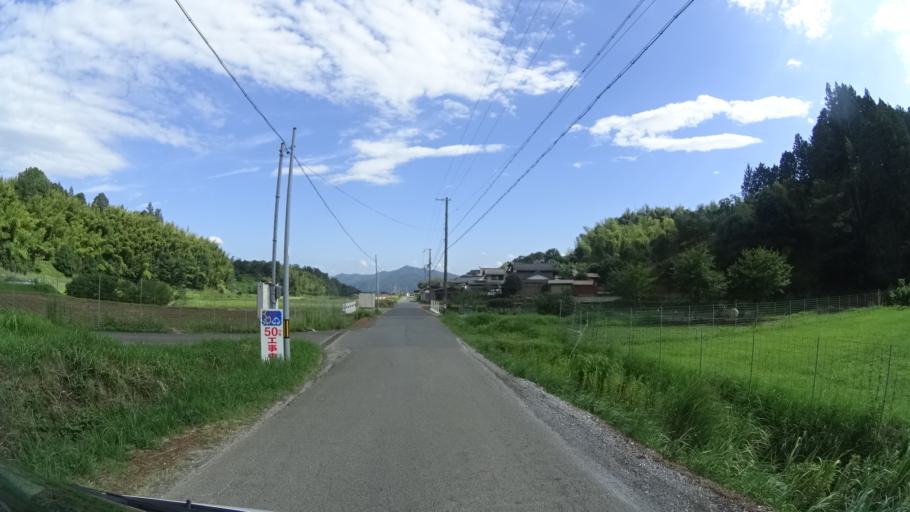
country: JP
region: Kyoto
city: Fukuchiyama
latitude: 35.3367
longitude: 135.1697
